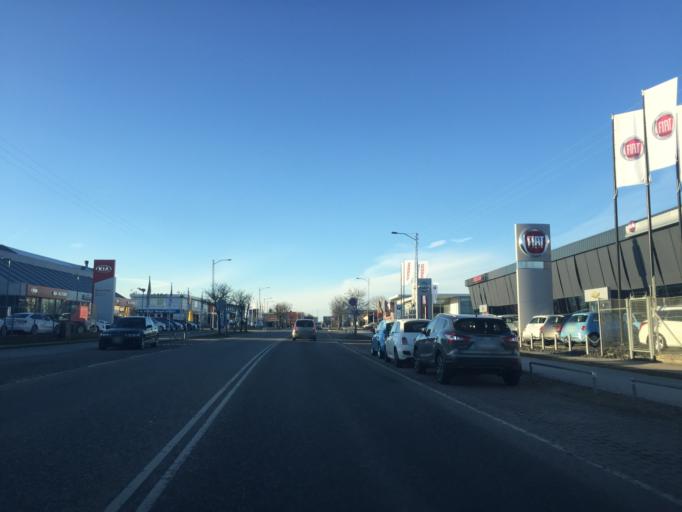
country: DK
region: Capital Region
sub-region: Tarnby Kommune
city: Tarnby
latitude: 55.6206
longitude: 12.6049
